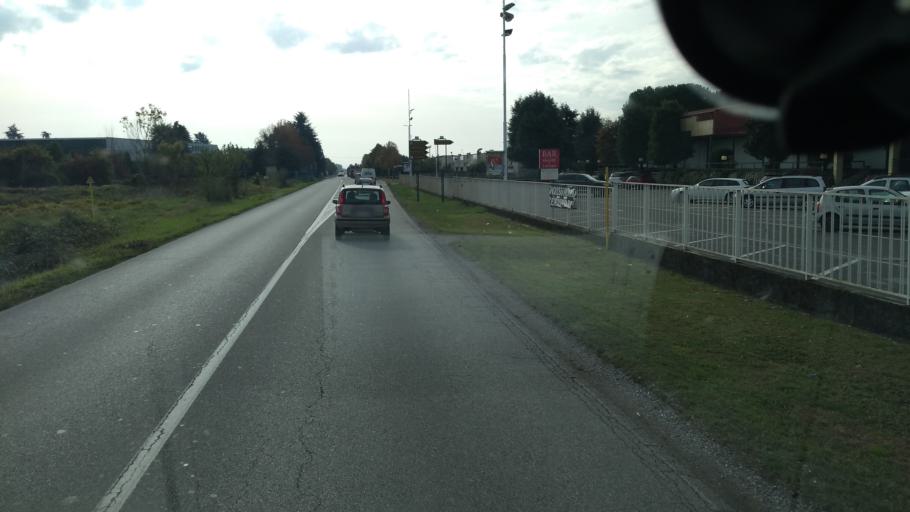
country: IT
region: Lombardy
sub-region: Provincia di Bergamo
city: Urgnano
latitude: 45.6148
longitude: 9.6933
